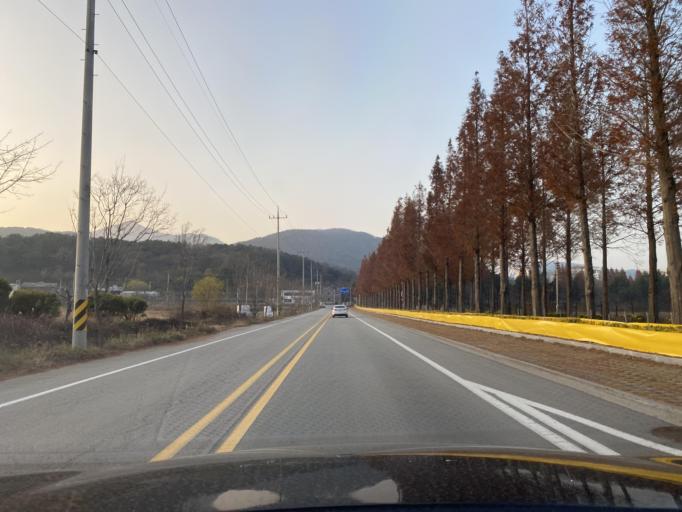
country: KR
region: Chungcheongnam-do
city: Hongsung
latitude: 36.6880
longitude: 126.6584
